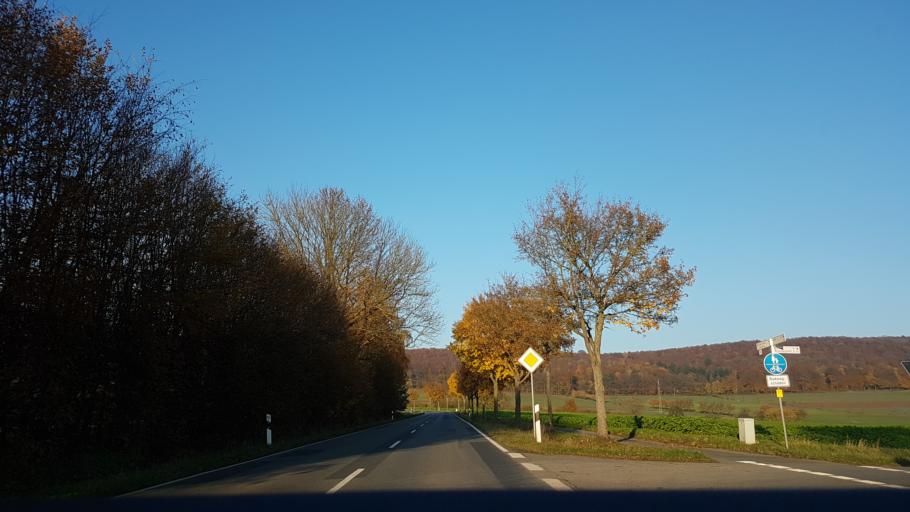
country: DE
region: Lower Saxony
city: Hameln
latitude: 52.1281
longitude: 9.3788
